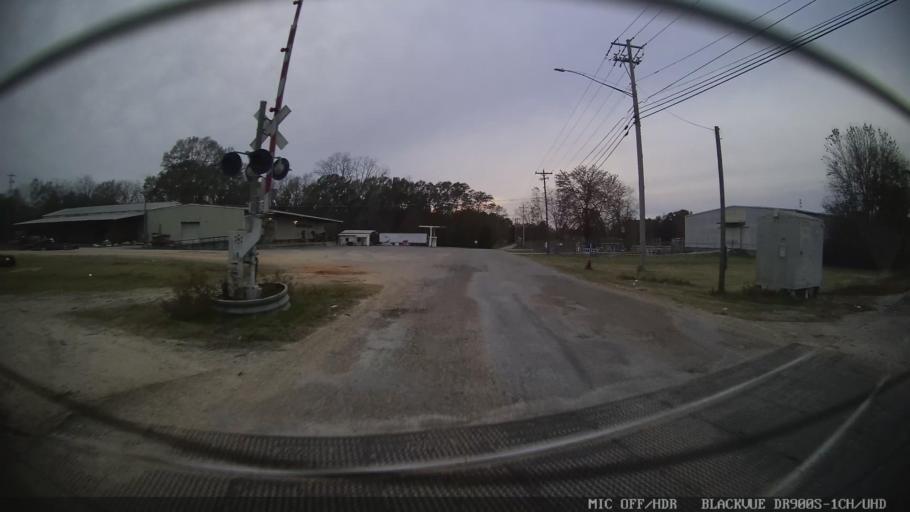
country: US
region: Mississippi
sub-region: Clarke County
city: Quitman
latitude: 32.0391
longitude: -88.7307
